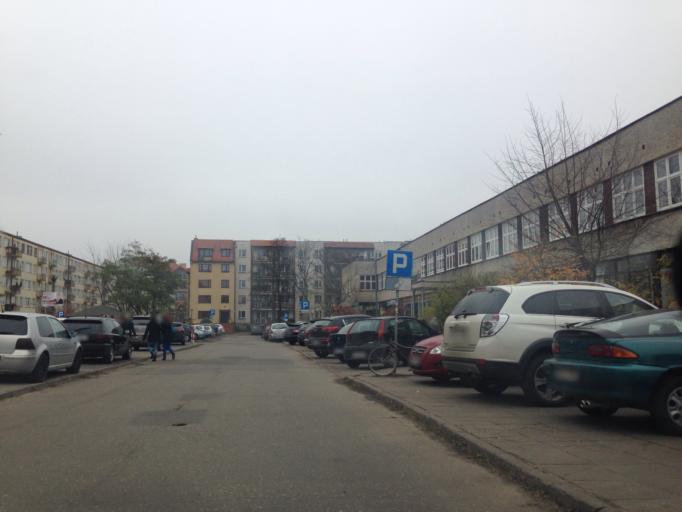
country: PL
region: Kujawsko-Pomorskie
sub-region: Torun
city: Torun
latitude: 53.0248
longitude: 18.6187
